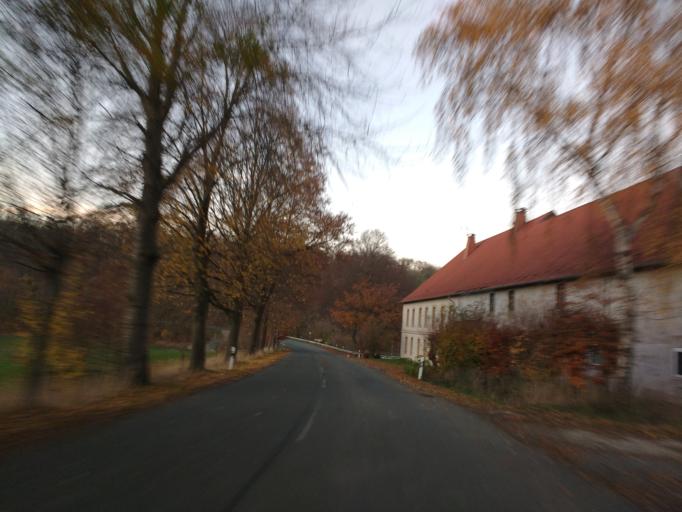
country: DE
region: North Rhine-Westphalia
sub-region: Regierungsbezirk Detmold
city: Paderborn
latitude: 51.6941
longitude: 8.7991
